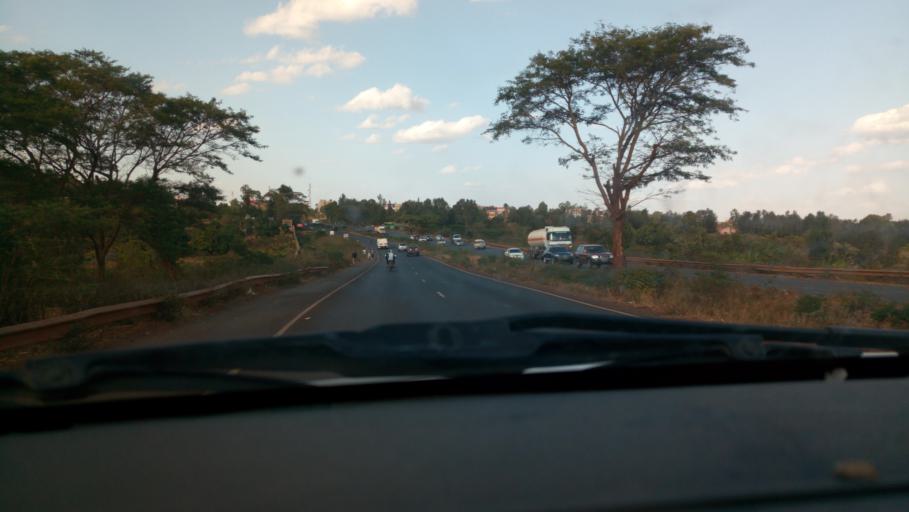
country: KE
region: Nairobi Area
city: Thika
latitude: -0.9466
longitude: 37.1189
